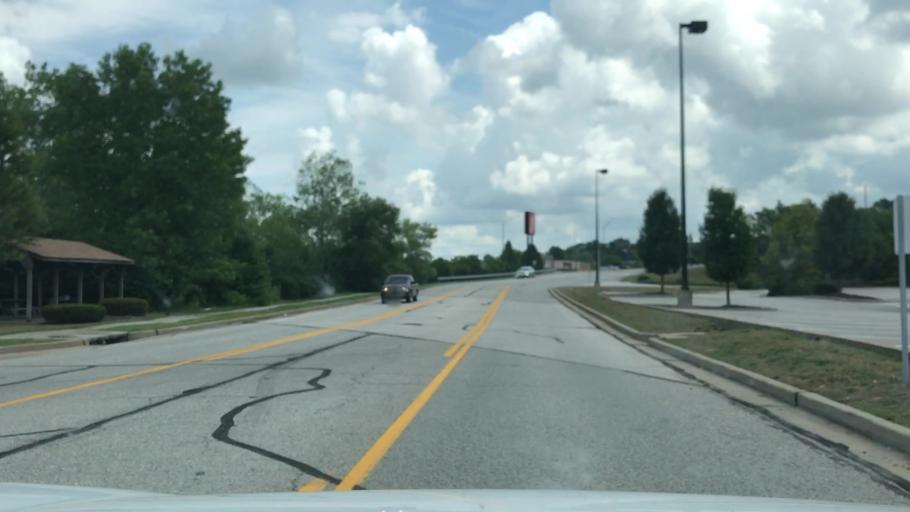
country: US
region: Missouri
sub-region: Saint Charles County
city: O'Fallon
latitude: 38.7899
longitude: -90.7018
